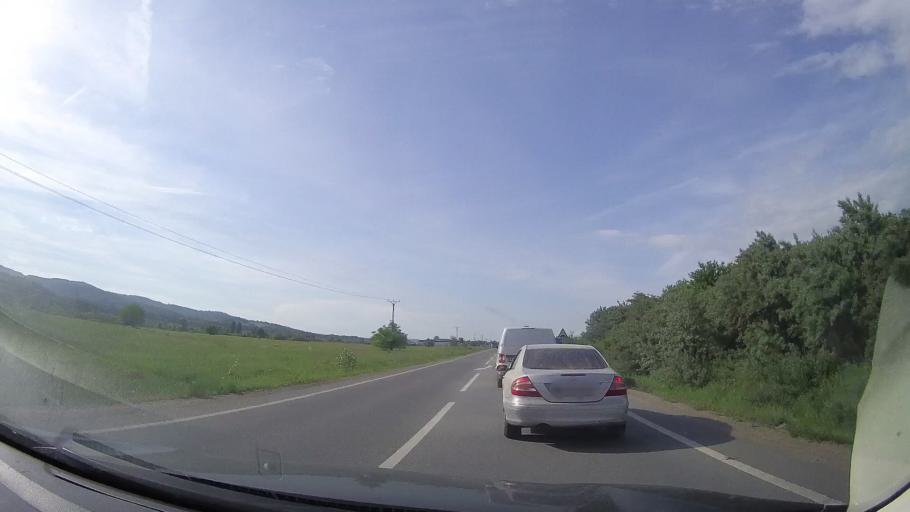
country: RO
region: Caras-Severin
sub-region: Comuna Buchin
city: Buchin
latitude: 45.3752
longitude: 22.2361
